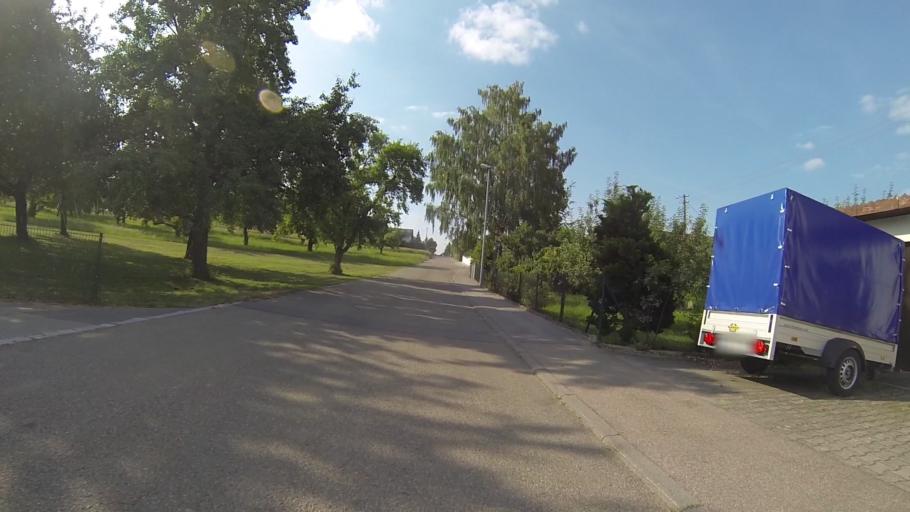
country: DE
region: Baden-Wuerttemberg
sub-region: Regierungsbezirk Stuttgart
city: Niederstotzingen
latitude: 48.5347
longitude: 10.2330
